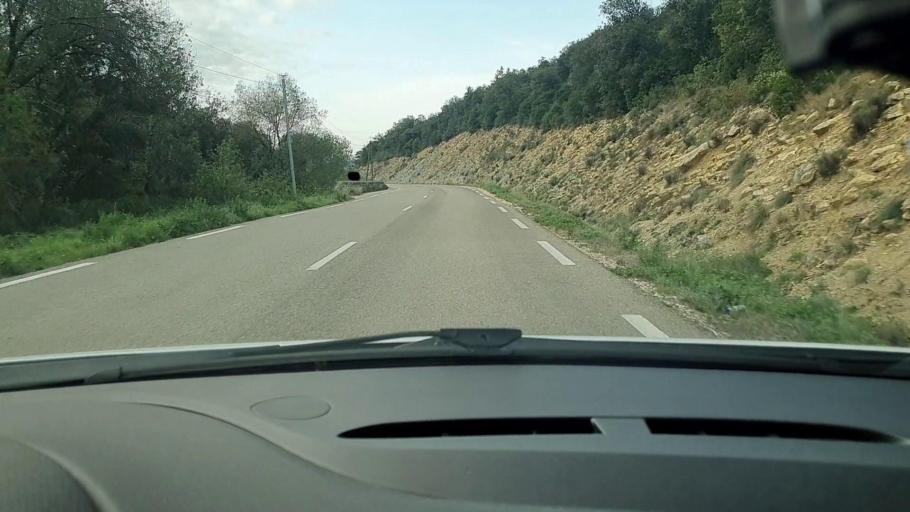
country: FR
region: Languedoc-Roussillon
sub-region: Departement du Gard
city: Mons
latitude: 44.0983
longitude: 4.2229
